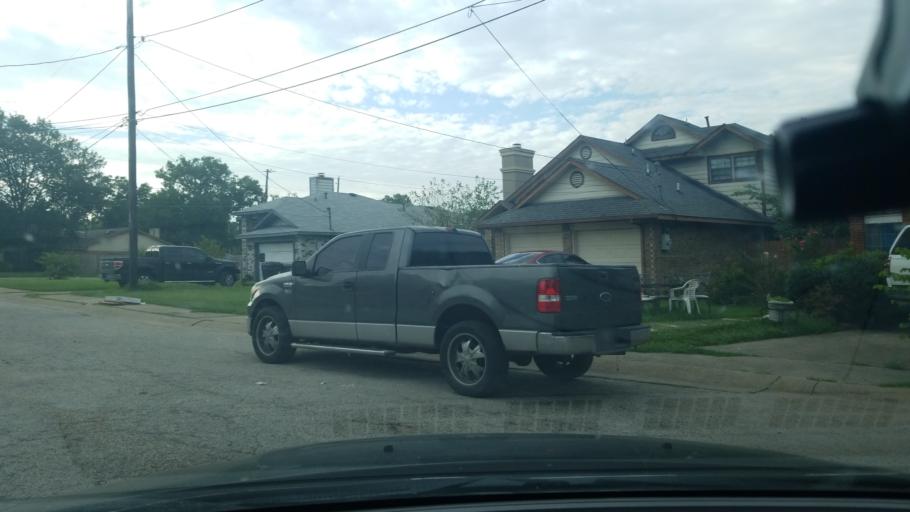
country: US
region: Texas
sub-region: Dallas County
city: Balch Springs
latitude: 32.7347
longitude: -96.6625
